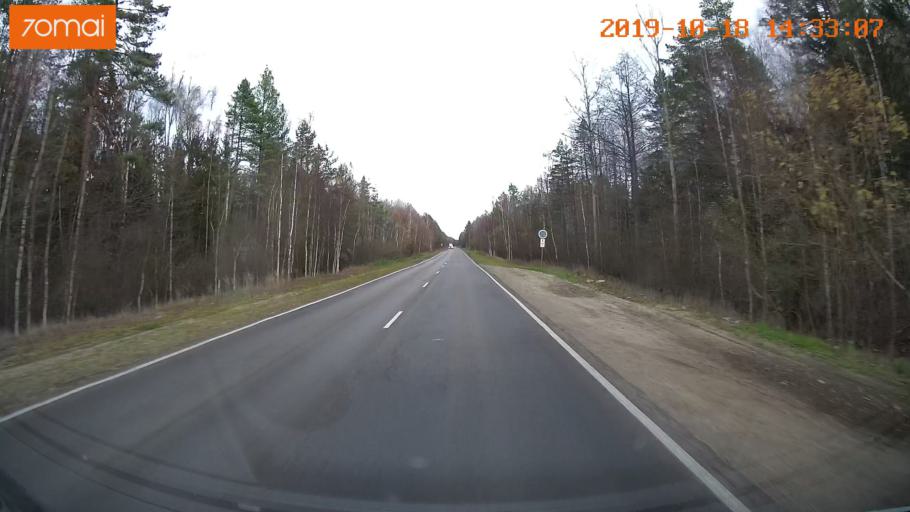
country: RU
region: Rjazan
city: Tuma
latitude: 55.1979
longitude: 40.5909
